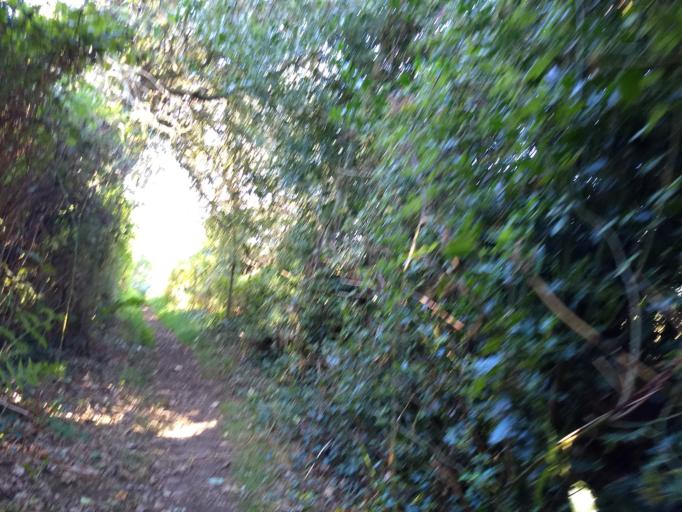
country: GB
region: England
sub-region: Isle of Wight
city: Niton
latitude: 50.6362
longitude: -1.2630
